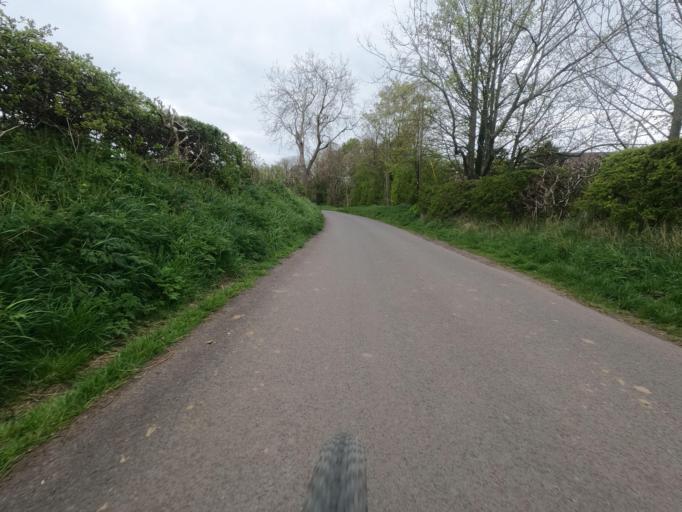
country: GB
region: England
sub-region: Northumberland
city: Ponteland
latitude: 55.0531
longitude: -1.7393
